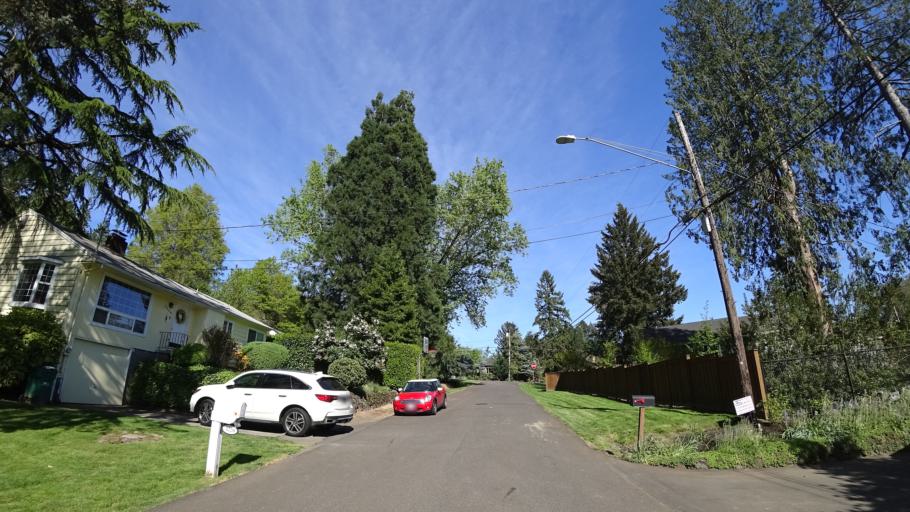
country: US
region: Oregon
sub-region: Washington County
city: West Slope
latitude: 45.4968
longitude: -122.7529
